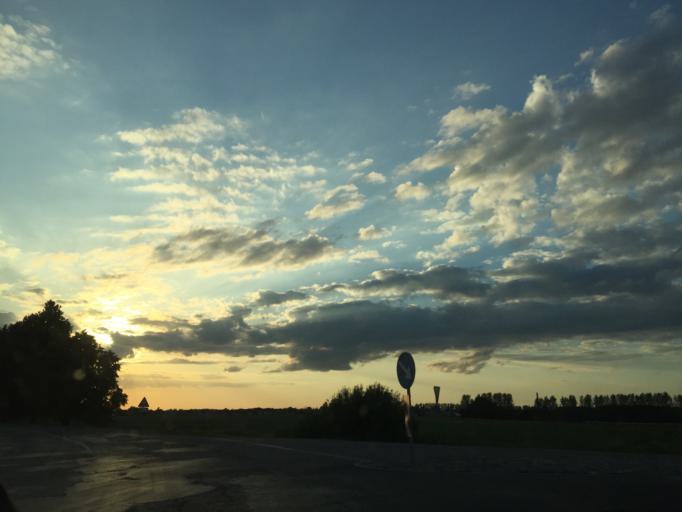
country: LV
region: Sigulda
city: Sigulda
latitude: 57.1370
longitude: 24.8938
